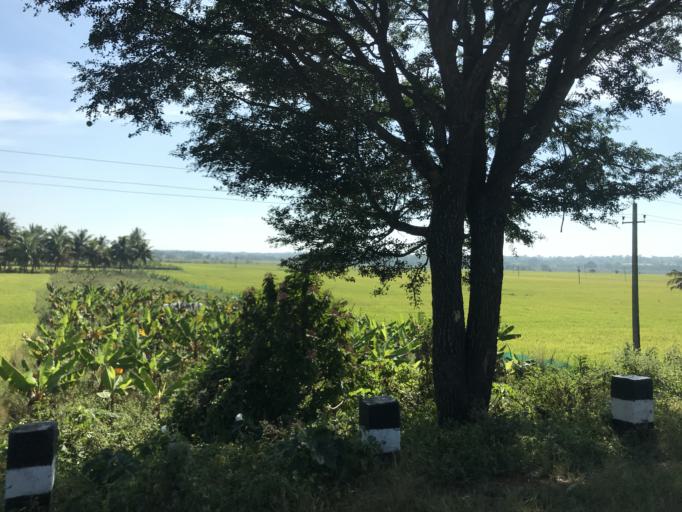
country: IN
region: Karnataka
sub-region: Mysore
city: Heggadadevankote
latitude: 12.1232
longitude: 76.4239
